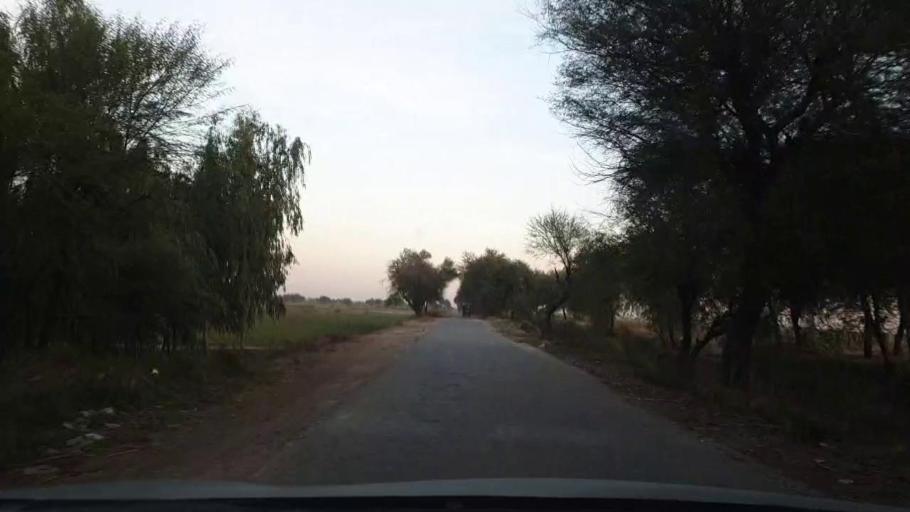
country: PK
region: Sindh
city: Tando Allahyar
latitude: 25.5991
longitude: 68.6975
